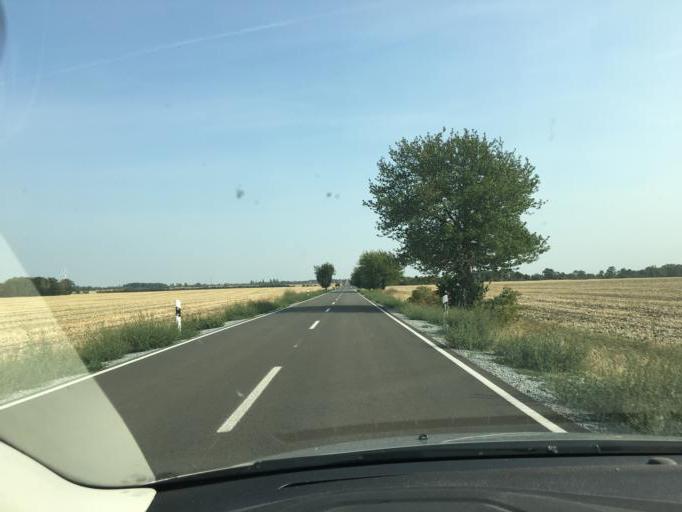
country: DE
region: Saxony-Anhalt
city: Baalberge
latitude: 51.8038
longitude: 11.8508
